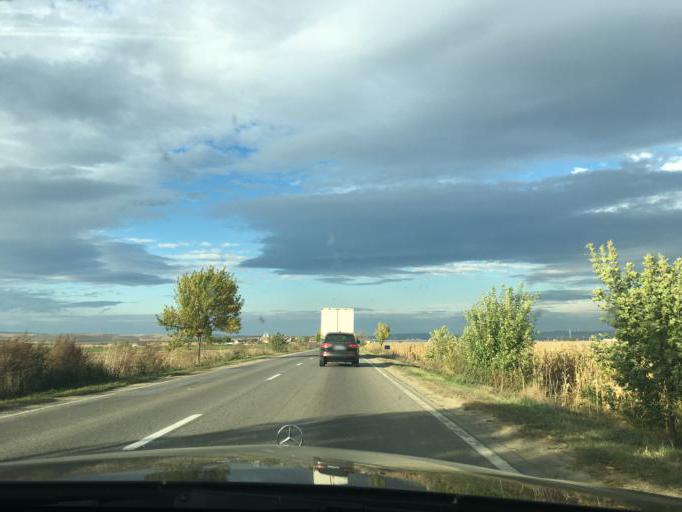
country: RO
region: Alba
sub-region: Comuna Galda de Jos
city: Galda de Jos
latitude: 46.1718
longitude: 23.6517
